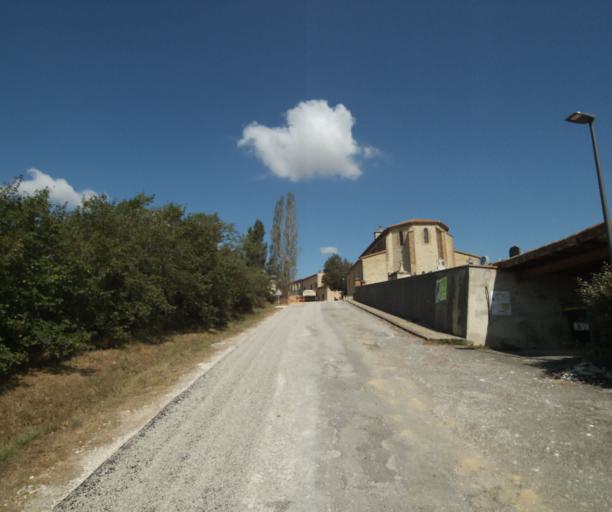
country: FR
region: Midi-Pyrenees
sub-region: Departement de la Haute-Garonne
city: Avignonet-Lauragais
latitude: 43.4483
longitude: 1.7909
